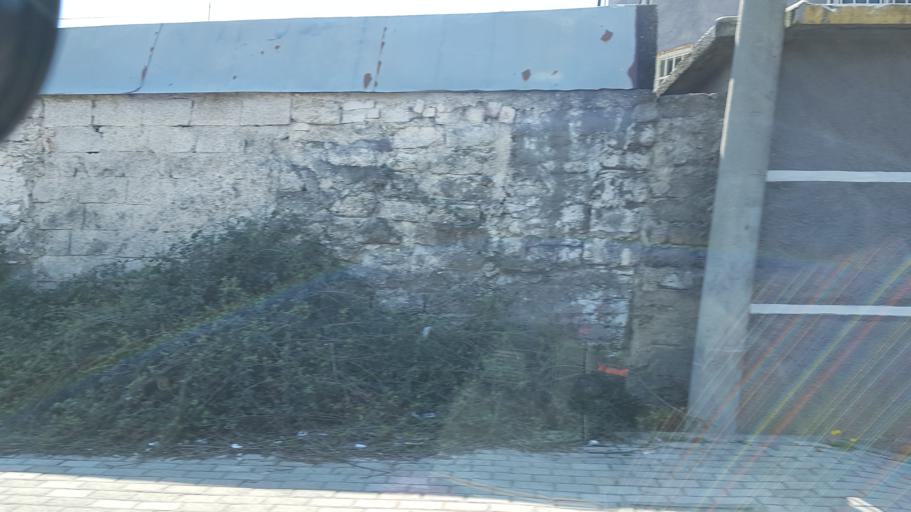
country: AL
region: Shkoder
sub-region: Rrethi i Shkodres
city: Shkoder
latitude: 42.0552
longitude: 19.5177
